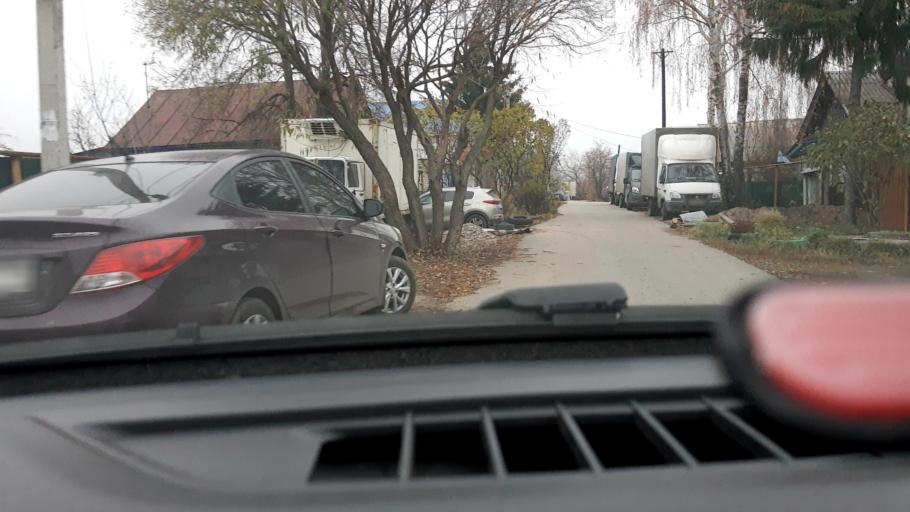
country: RU
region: Nizjnij Novgorod
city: Gorbatovka
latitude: 56.2759
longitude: 43.8772
